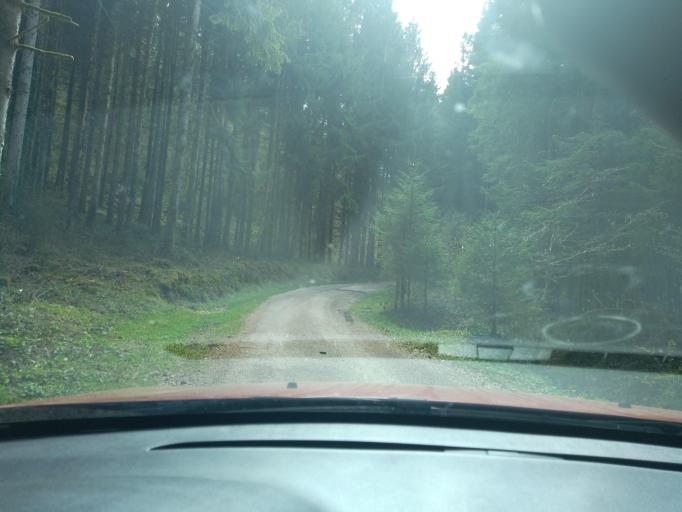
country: FR
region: Franche-Comte
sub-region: Departement du Jura
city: Moirans-en-Montagne
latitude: 46.4508
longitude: 5.7330
